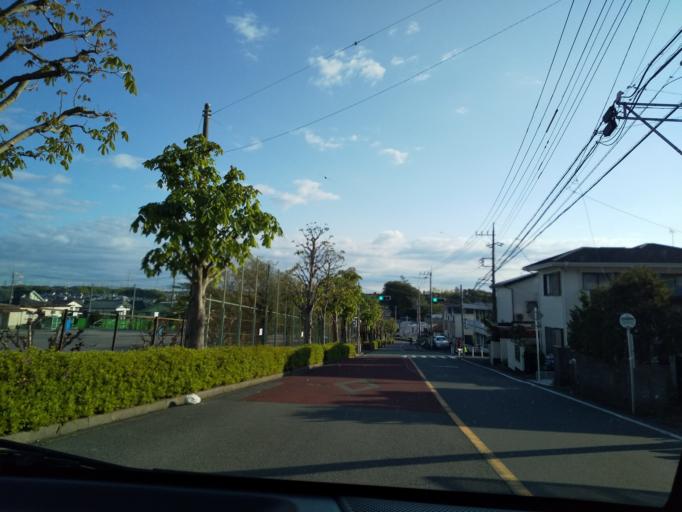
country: JP
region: Tokyo
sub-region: Machida-shi
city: Machida
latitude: 35.5696
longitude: 139.4588
